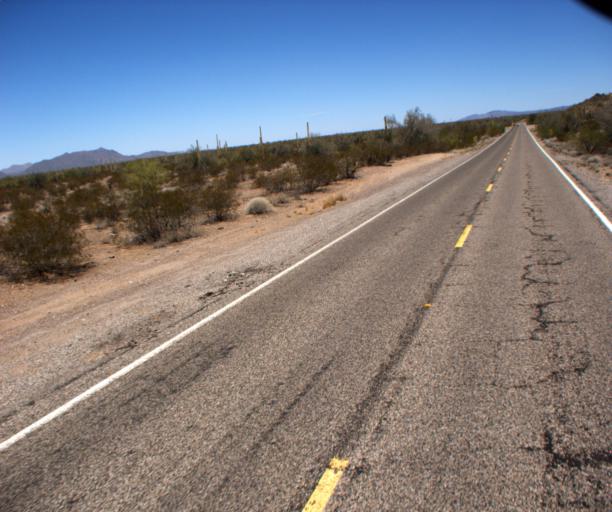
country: US
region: Arizona
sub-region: Pima County
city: Ajo
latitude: 32.2101
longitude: -112.7582
